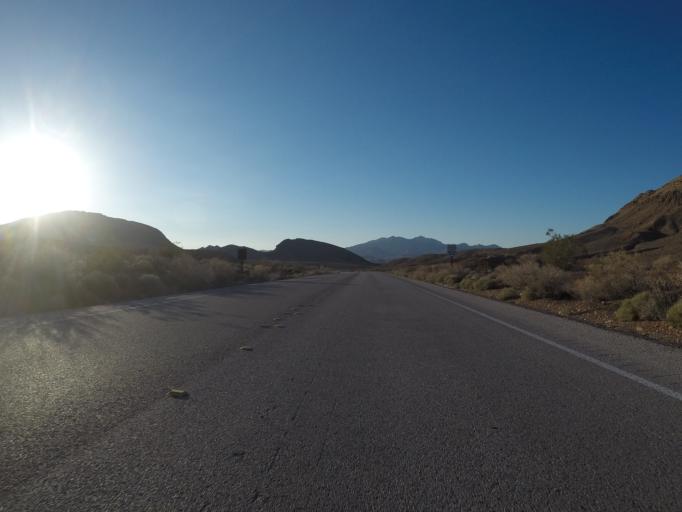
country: US
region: Nevada
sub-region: Clark County
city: Moapa Valley
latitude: 36.2431
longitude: -114.5348
